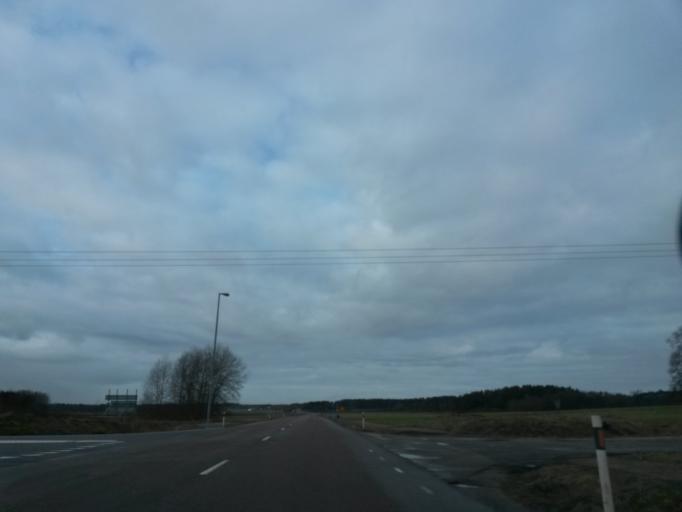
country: SE
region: Vaestra Goetaland
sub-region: Vargarda Kommun
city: Vargarda
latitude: 58.0429
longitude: 12.7970
